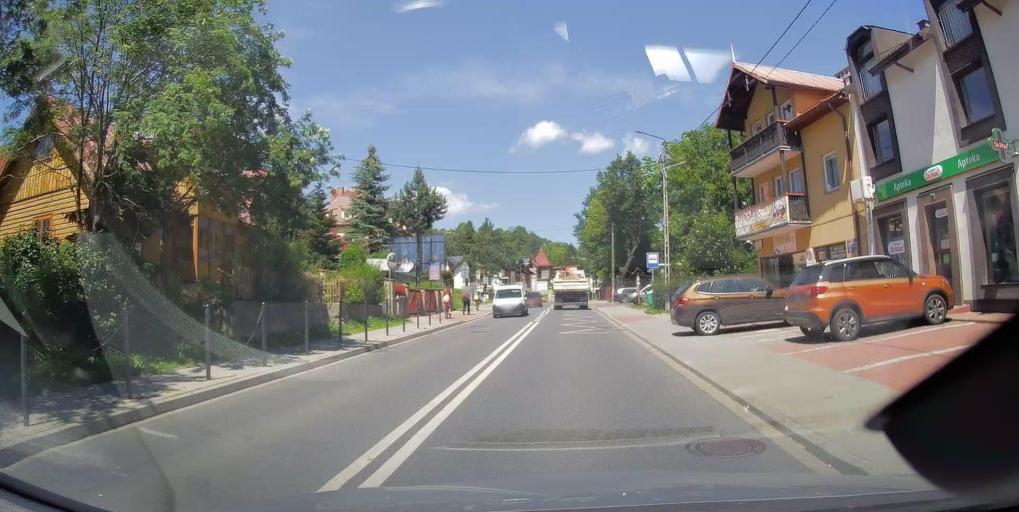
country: PL
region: Lesser Poland Voivodeship
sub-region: Powiat nowosadecki
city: Krynica-Zdroj
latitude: 49.4054
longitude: 20.9532
